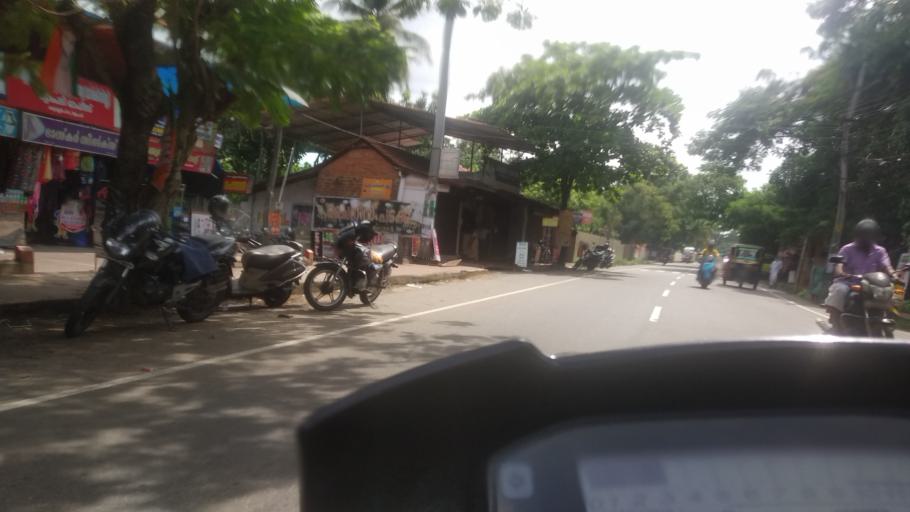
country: IN
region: Kerala
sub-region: Ernakulam
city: Elur
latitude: 10.1310
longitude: 76.2827
